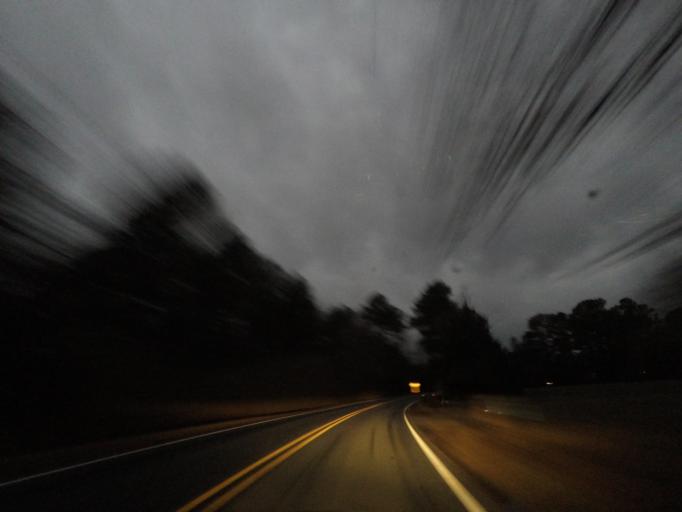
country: US
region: North Carolina
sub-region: Orange County
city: Hillsborough
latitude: 36.0667
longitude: -78.9937
